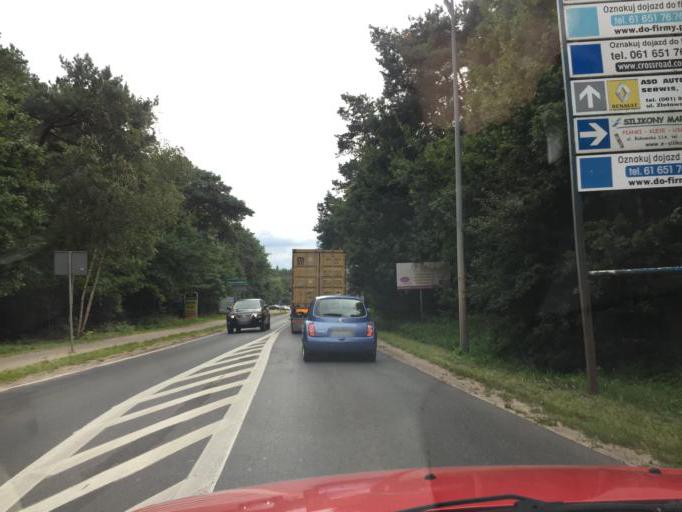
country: PL
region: Greater Poland Voivodeship
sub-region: Powiat poznanski
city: Baranowo
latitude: 52.4165
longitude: 16.7897
